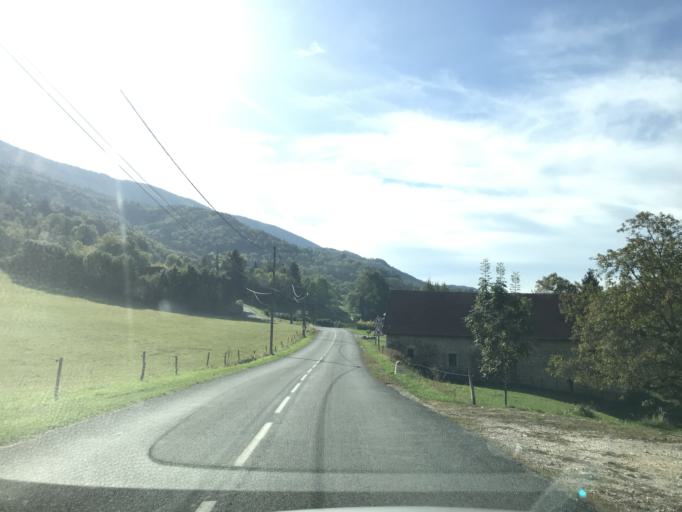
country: FR
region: Rhone-Alpes
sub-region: Departement de la Savoie
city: Yenne
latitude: 45.6528
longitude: 5.7891
